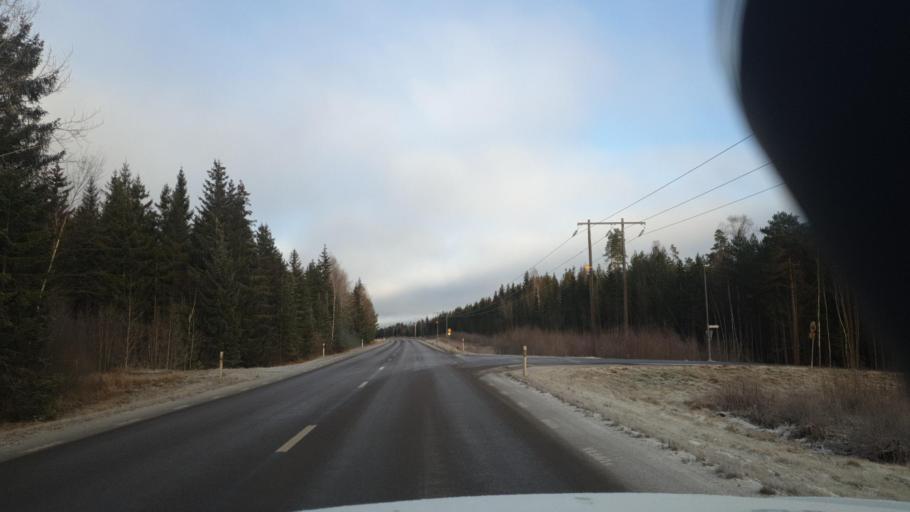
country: SE
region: Vaermland
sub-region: Karlstads Kommun
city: Edsvalla
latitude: 59.4306
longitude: 13.1988
